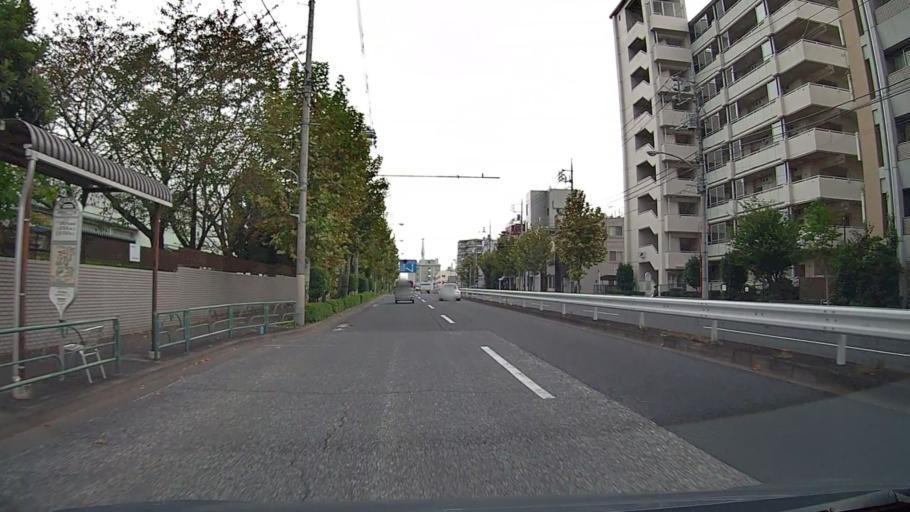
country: JP
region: Saitama
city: Wako
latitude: 35.7616
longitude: 139.6598
